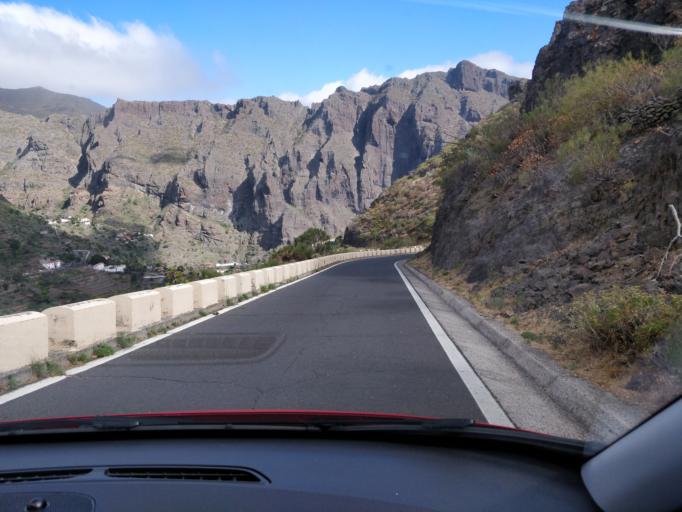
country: ES
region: Canary Islands
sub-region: Provincia de Santa Cruz de Tenerife
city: Santiago del Teide
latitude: 28.3103
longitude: -16.8467
